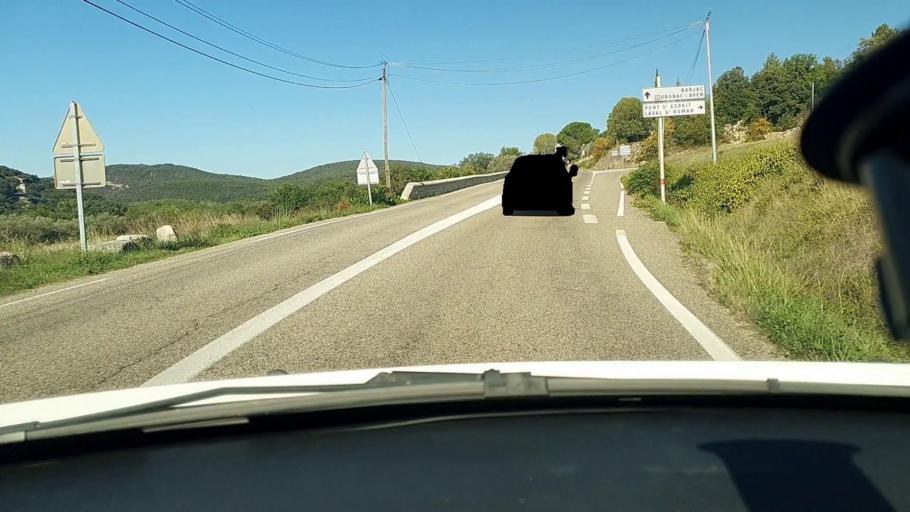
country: FR
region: Languedoc-Roussillon
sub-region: Departement du Gard
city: Goudargues
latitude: 44.2692
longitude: 4.4266
